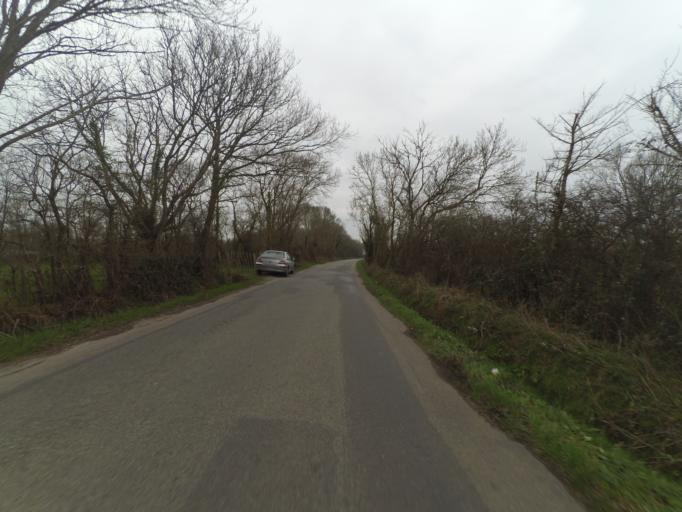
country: FR
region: Pays de la Loire
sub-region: Departement de la Loire-Atlantique
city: Indre
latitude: 47.2279
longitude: -1.6841
